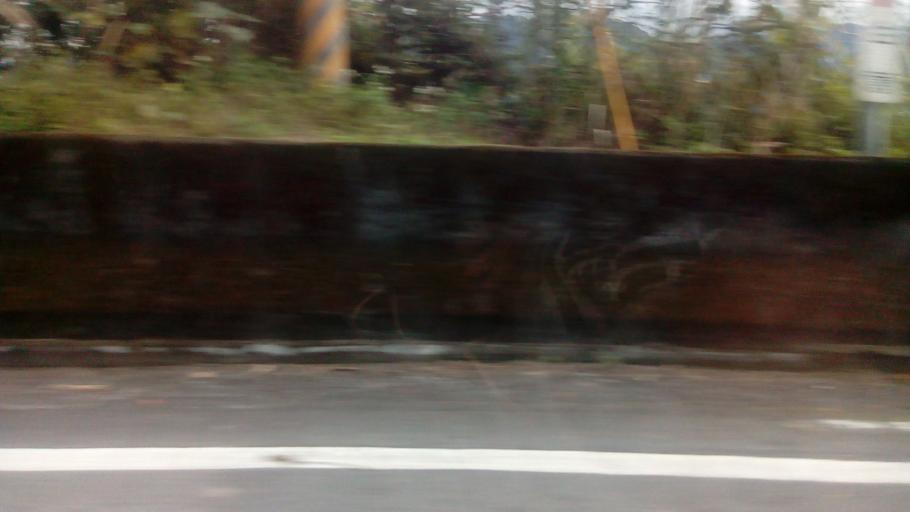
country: TW
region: Taiwan
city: Daxi
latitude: 24.4612
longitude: 121.3946
